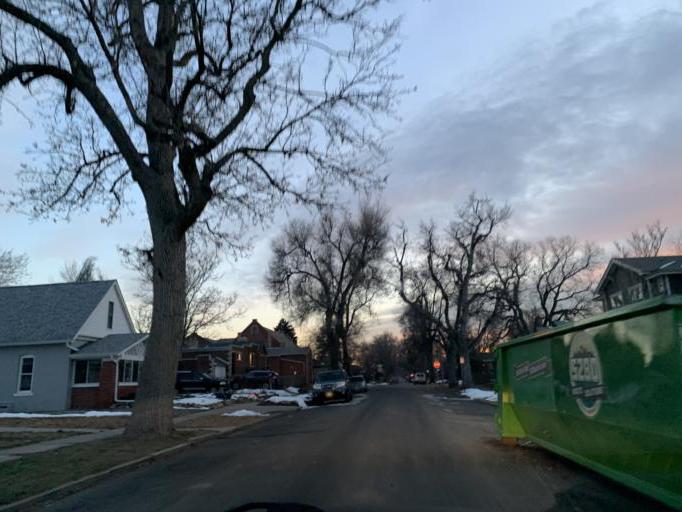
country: US
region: Colorado
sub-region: Adams County
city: Berkley
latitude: 39.7775
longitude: -105.0404
